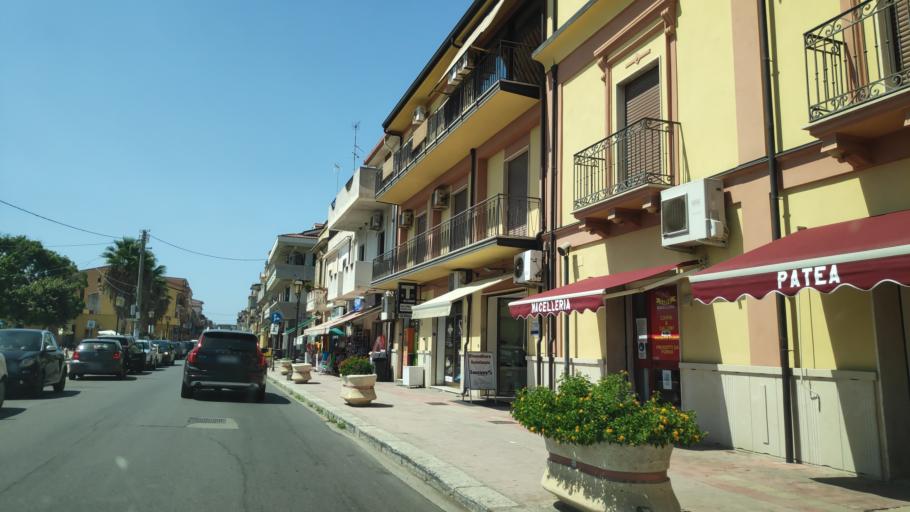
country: IT
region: Calabria
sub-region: Provincia di Reggio Calabria
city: Brancaleone-Marina
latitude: 37.9663
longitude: 16.1033
